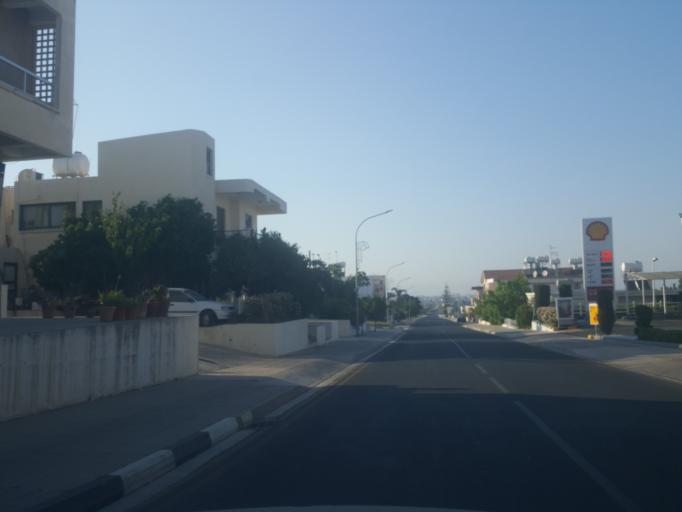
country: CY
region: Ammochostos
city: Deryneia
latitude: 35.0677
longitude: 33.9608
